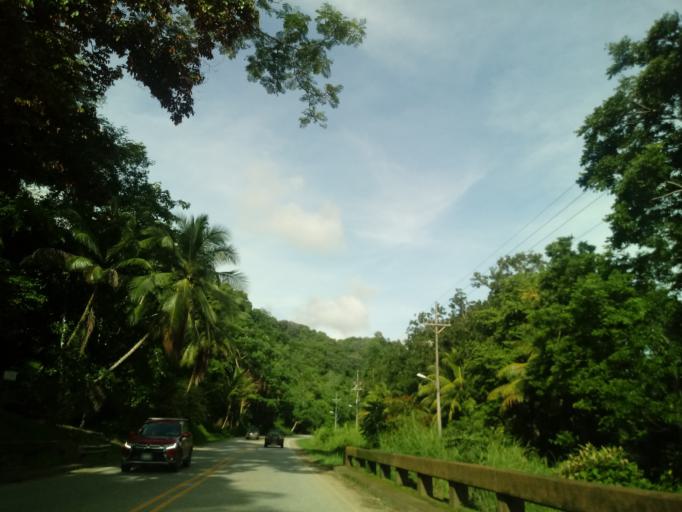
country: CR
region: San Jose
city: Daniel Flores
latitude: 9.2053
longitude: -83.7979
